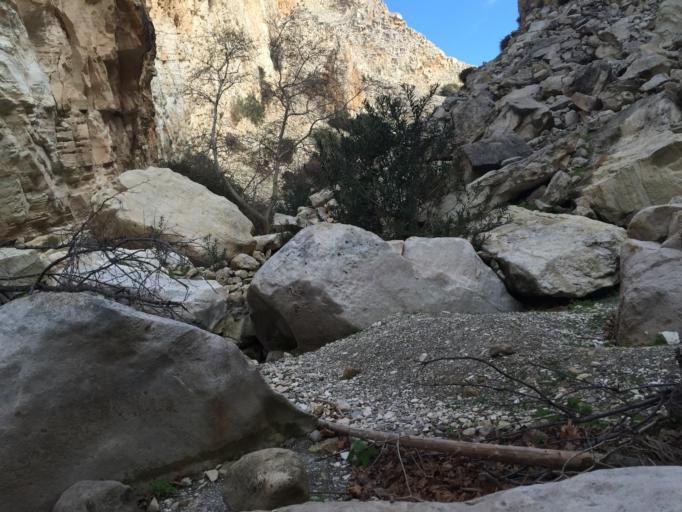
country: CY
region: Pafos
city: Pegeia
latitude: 34.9257
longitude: 32.3491
